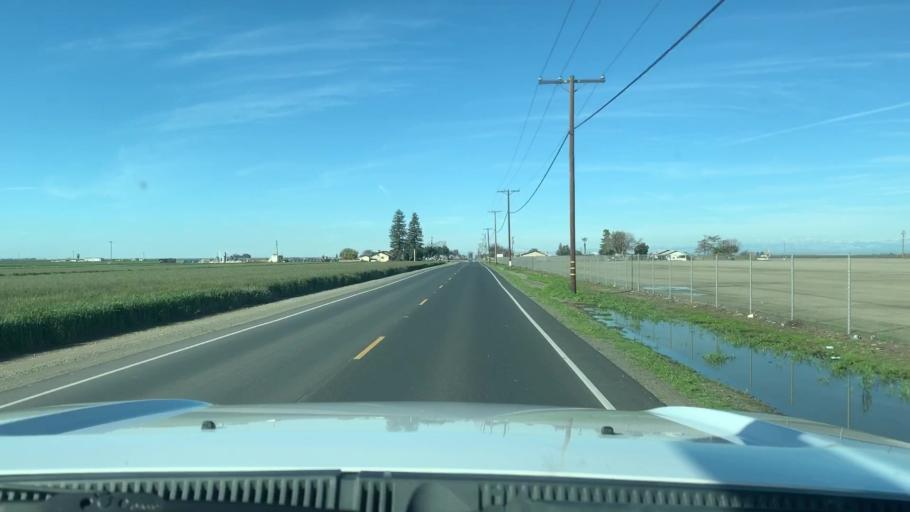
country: US
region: California
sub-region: Kings County
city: Corcoran
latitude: 36.1854
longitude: -119.4933
